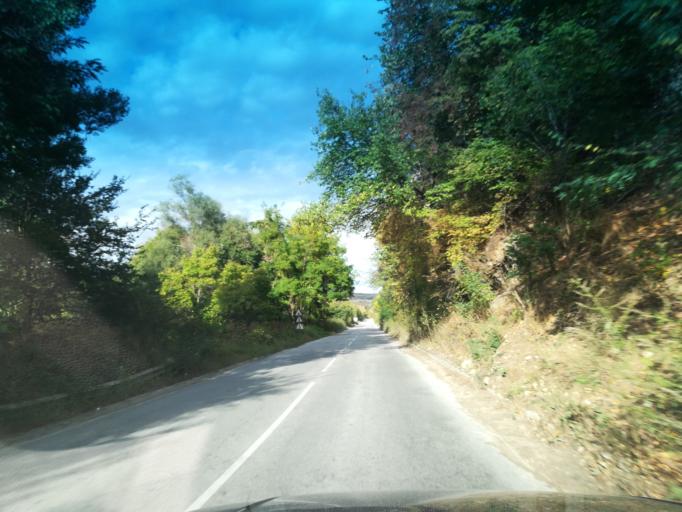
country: BG
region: Pazardzhik
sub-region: Obshtina Bratsigovo
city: Bratsigovo
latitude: 42.0536
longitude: 24.3418
